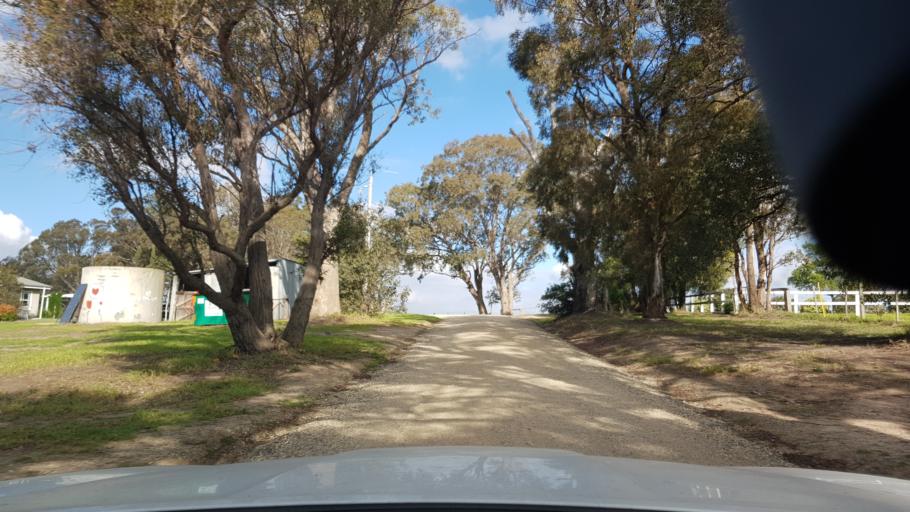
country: AU
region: Victoria
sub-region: East Gippsland
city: Bairnsdale
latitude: -37.7818
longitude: 147.5750
